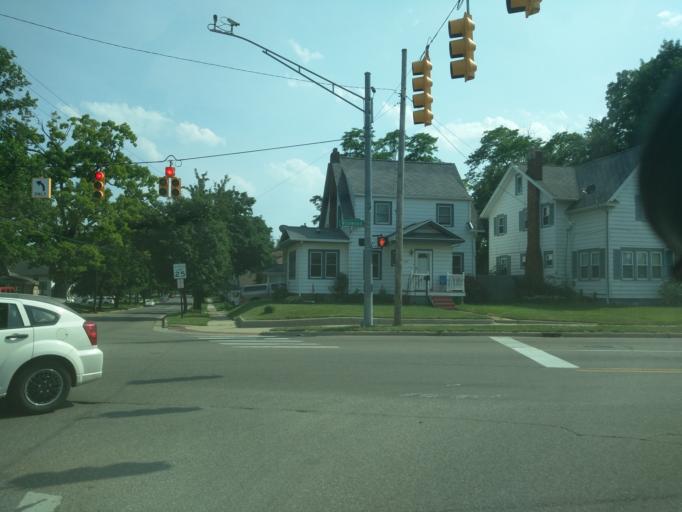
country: US
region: Michigan
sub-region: Jackson County
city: Jackson
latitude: 42.2519
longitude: -84.4284
